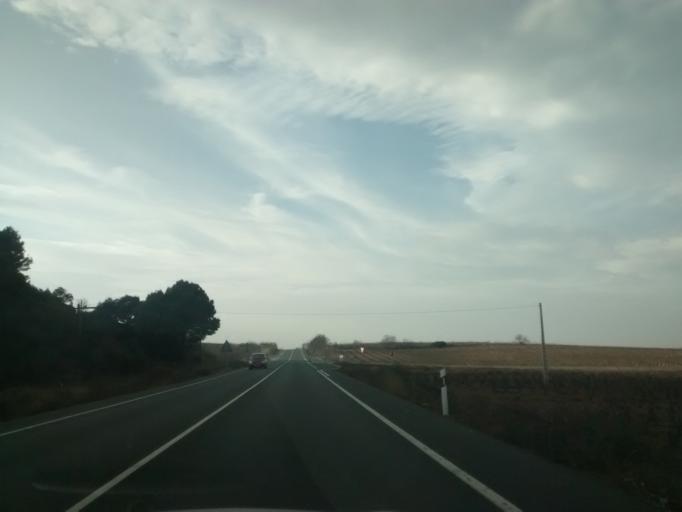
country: ES
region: La Rioja
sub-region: Provincia de La Rioja
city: Torremontalbo
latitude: 42.5066
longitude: -2.6958
